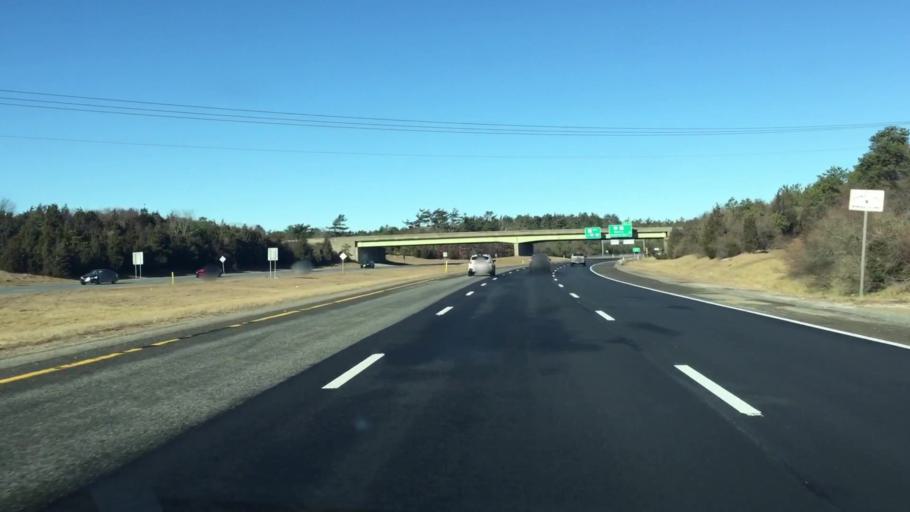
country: US
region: Massachusetts
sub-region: Barnstable County
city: Bourne
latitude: 41.7548
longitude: -70.5934
